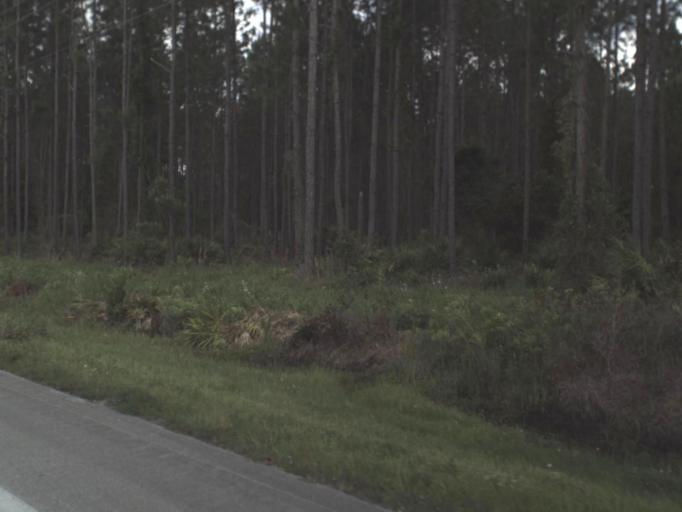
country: US
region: Florida
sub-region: Saint Johns County
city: Saint Augustine Shores
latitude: 29.7529
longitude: -81.3347
